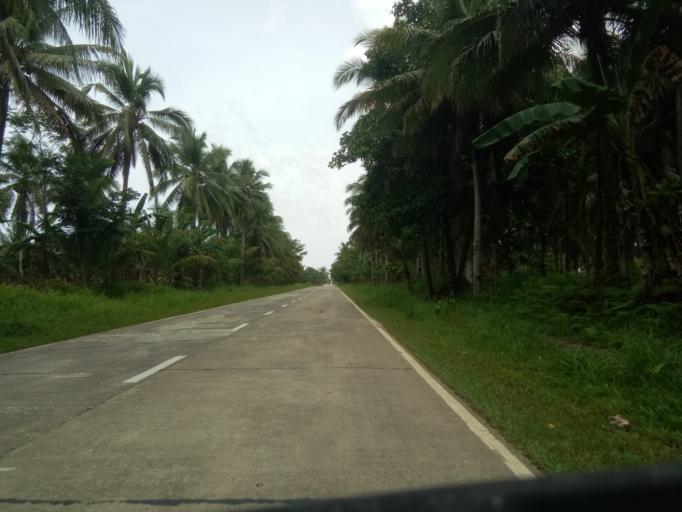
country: PH
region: Caraga
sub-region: Province of Surigao del Norte
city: San Isidro
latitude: 9.9235
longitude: 126.0511
